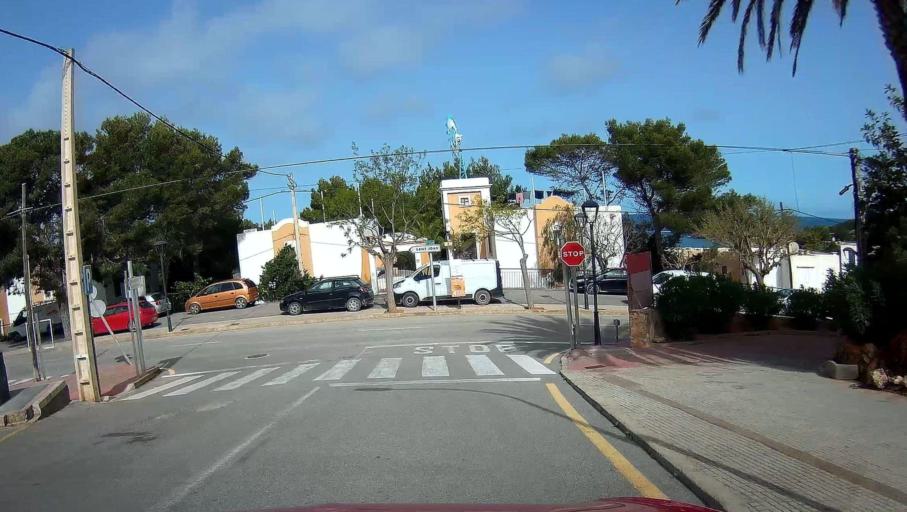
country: ES
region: Balearic Islands
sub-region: Illes Balears
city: Sant Joan de Labritja
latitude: 39.1123
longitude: 1.5181
